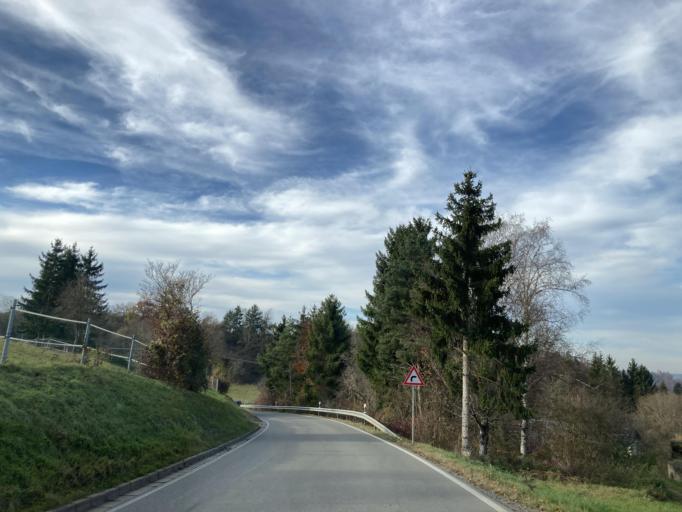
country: DE
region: Baden-Wuerttemberg
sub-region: Tuebingen Region
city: Haigerloch
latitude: 48.4361
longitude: 8.8093
